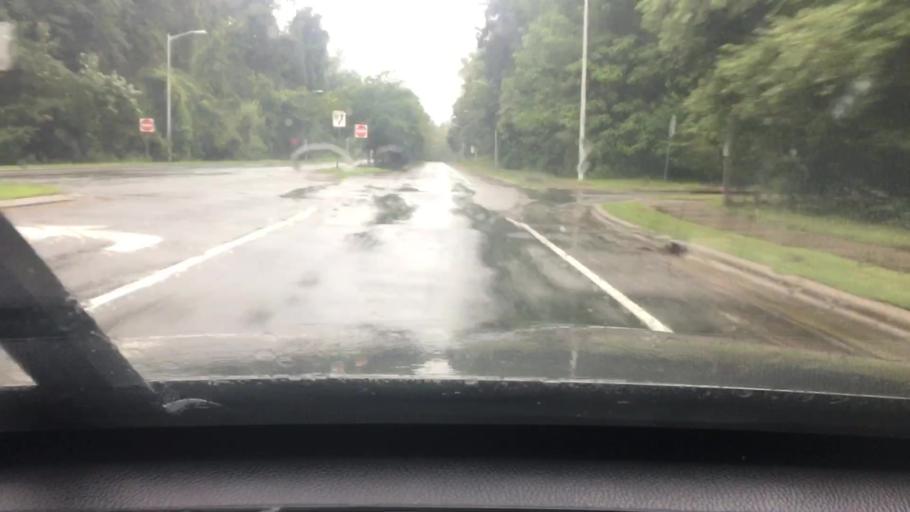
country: US
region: North Carolina
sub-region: Alamance County
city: Burlington
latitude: 36.0888
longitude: -79.4619
